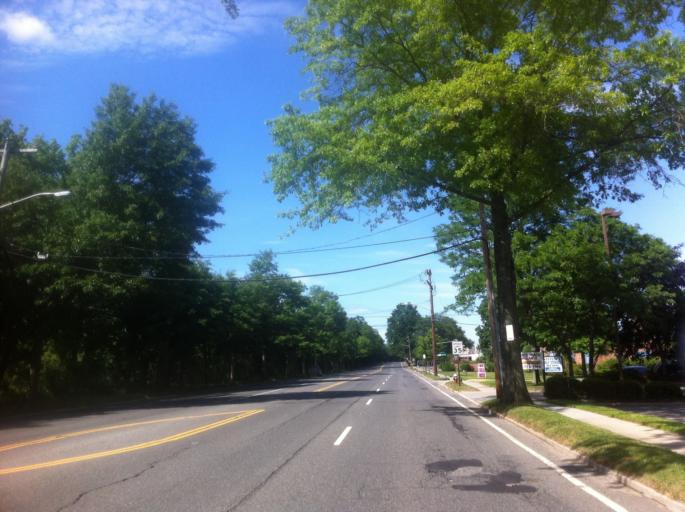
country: US
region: New York
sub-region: Nassau County
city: Syosset
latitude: 40.8136
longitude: -73.5135
